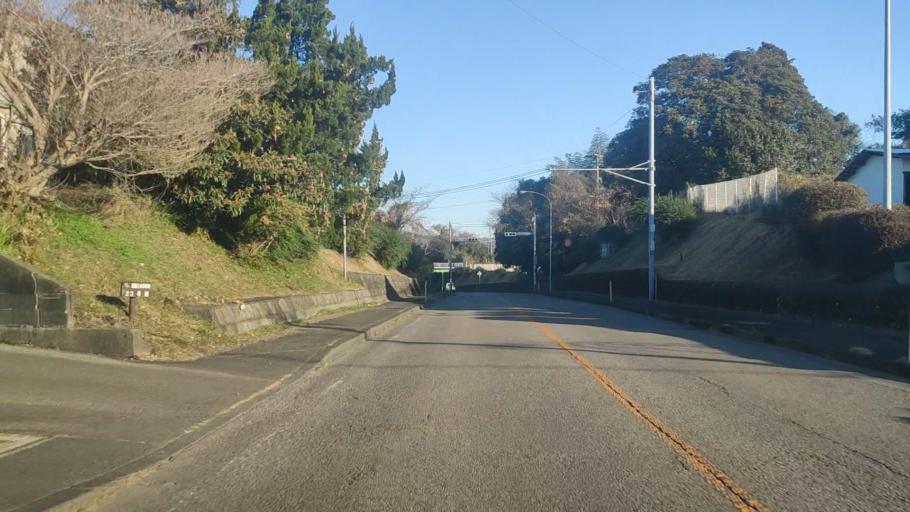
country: JP
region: Miyazaki
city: Takanabe
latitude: 32.2336
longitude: 131.5486
